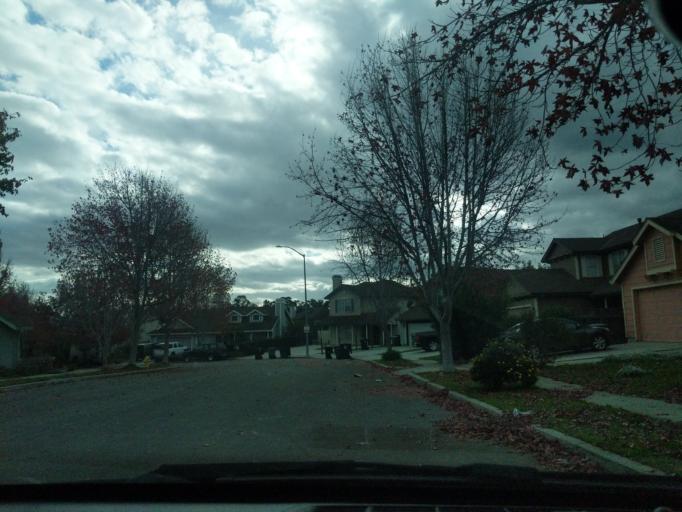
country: US
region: California
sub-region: Monterey County
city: Salinas
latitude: 36.7124
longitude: -121.6210
